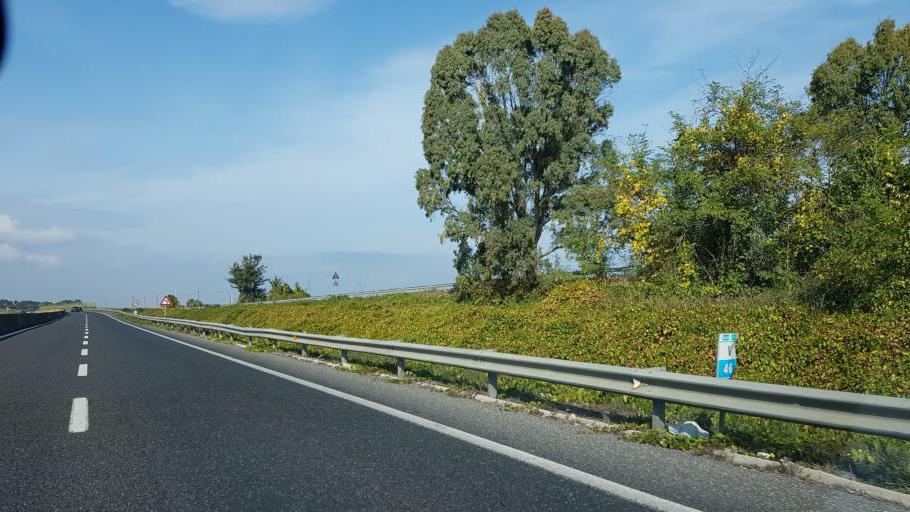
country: IT
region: Apulia
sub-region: Provincia di Brindisi
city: Brindisi
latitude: 40.6656
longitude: 17.8754
